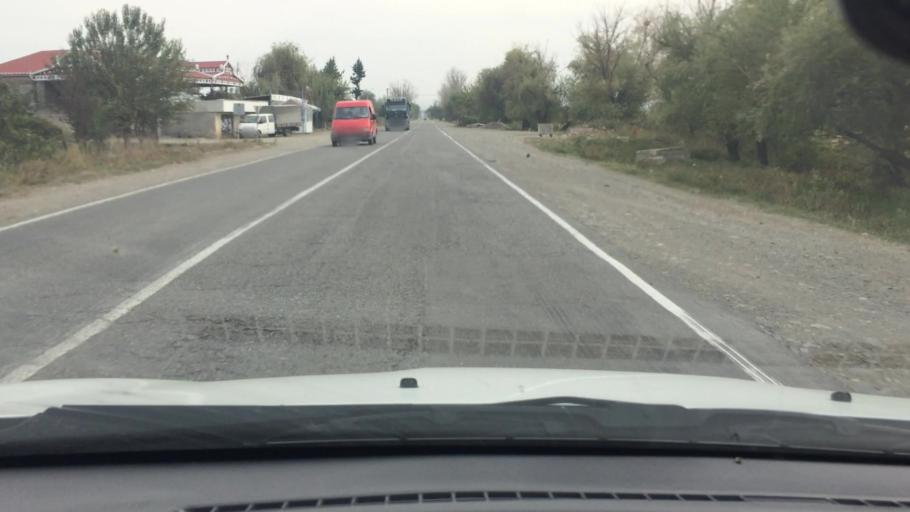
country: GE
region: Kvemo Kartli
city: Rust'avi
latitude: 41.4501
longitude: 44.9939
